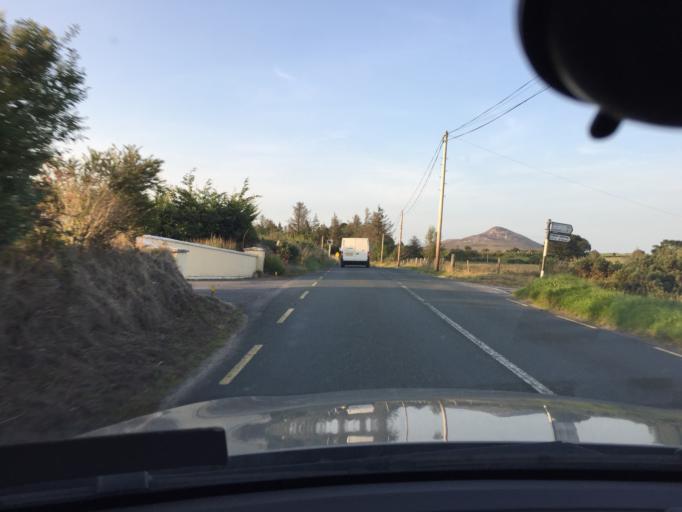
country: IE
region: Leinster
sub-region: Wicklow
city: Kilmacanoge
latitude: 53.1256
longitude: -6.1818
